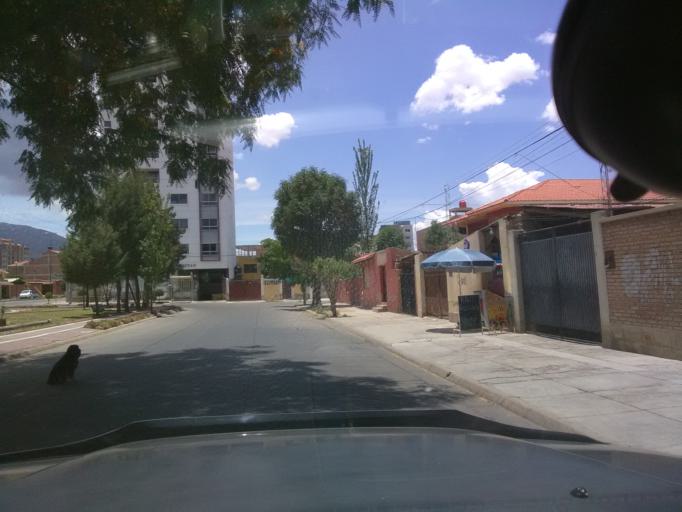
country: BO
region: Cochabamba
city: Cochabamba
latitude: -17.3795
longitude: -66.1792
